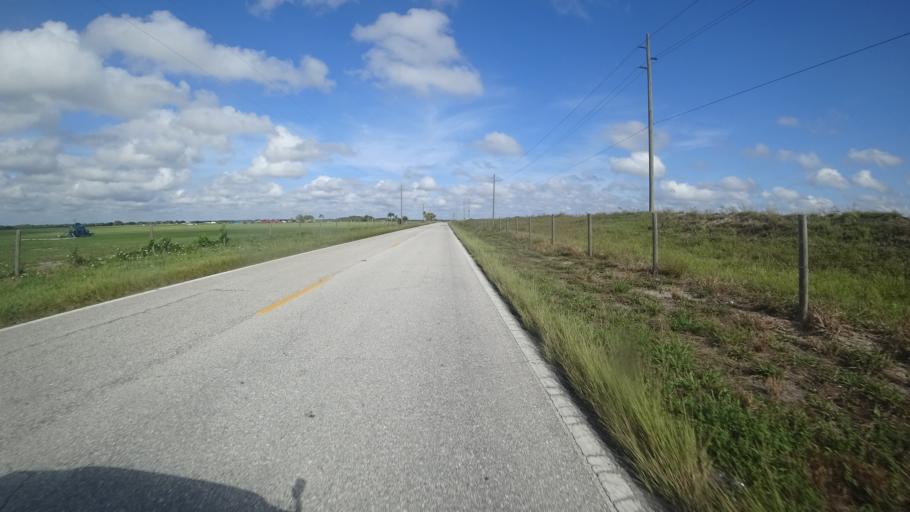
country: US
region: Florida
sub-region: Hardee County
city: Wauchula
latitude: 27.5249
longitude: -82.0750
